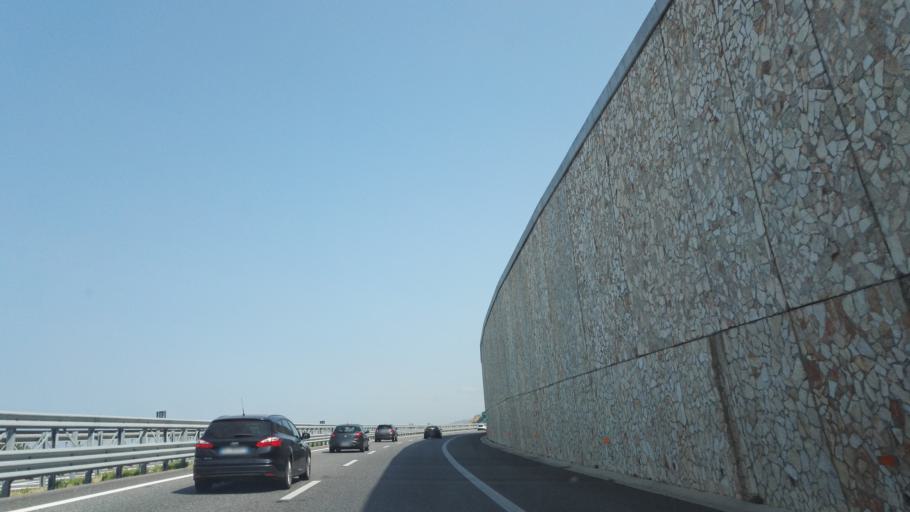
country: IT
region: Calabria
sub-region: Provincia di Catanzaro
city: Nocera Scalo
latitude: 39.0182
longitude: 16.1222
